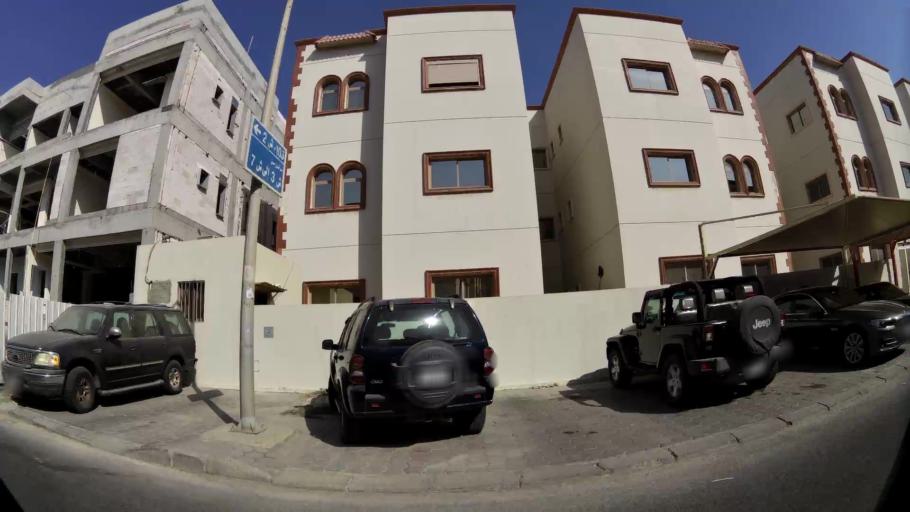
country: KW
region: Muhafazat Hawalli
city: Salwa
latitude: 29.2899
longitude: 48.0849
